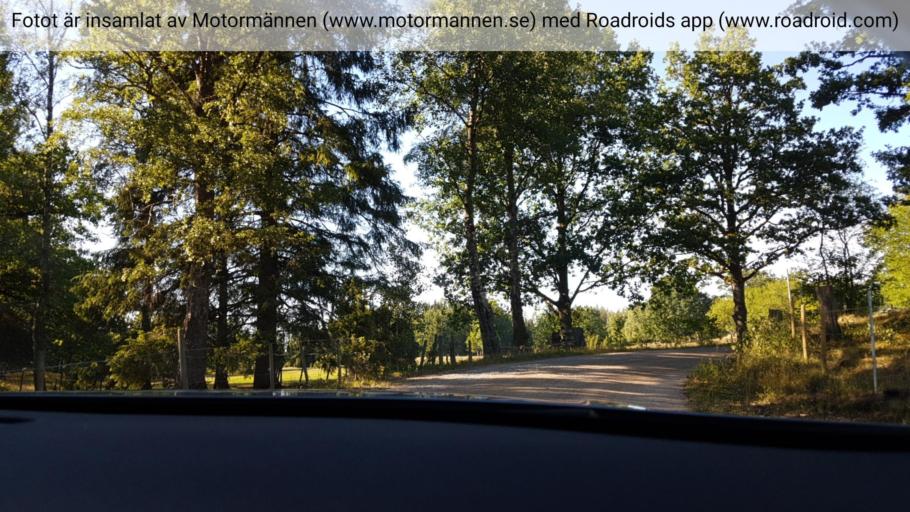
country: SE
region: Joenkoeping
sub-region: Vaggeryds Kommun
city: Skillingaryd
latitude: 57.3460
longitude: 14.0461
